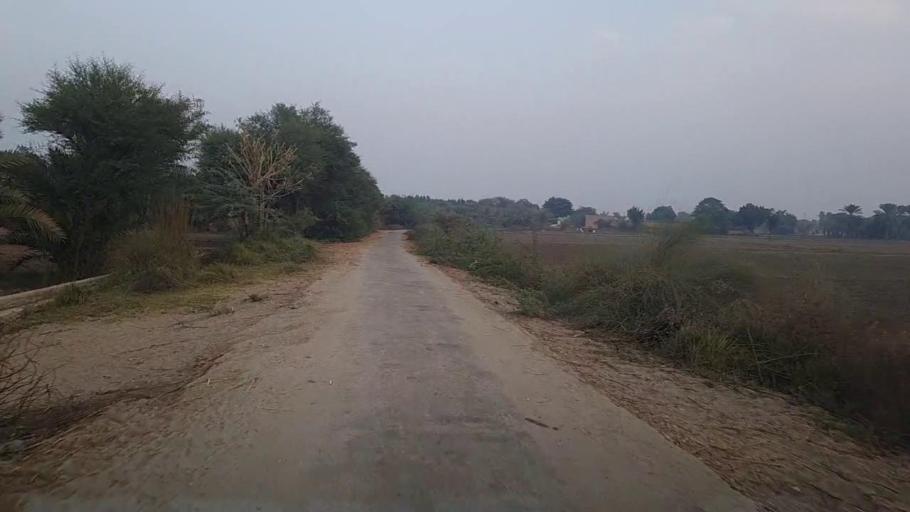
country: PK
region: Sindh
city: Kot Diji
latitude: 27.3455
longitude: 68.6380
